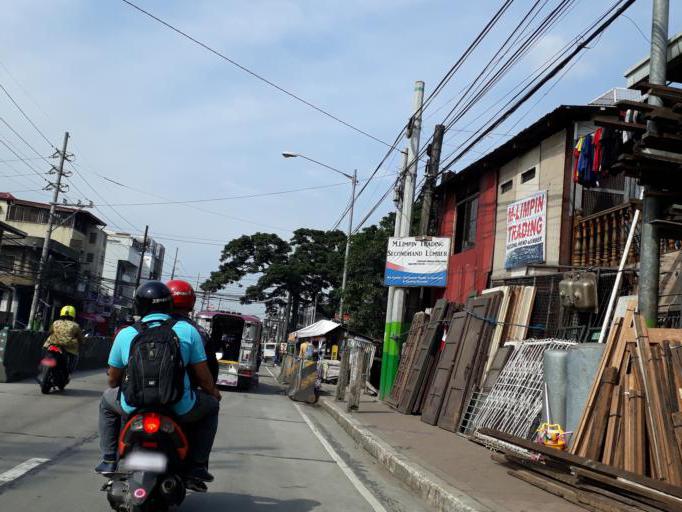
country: PH
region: Calabarzon
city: Bagong Pagasa
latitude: 14.6717
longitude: 121.0118
